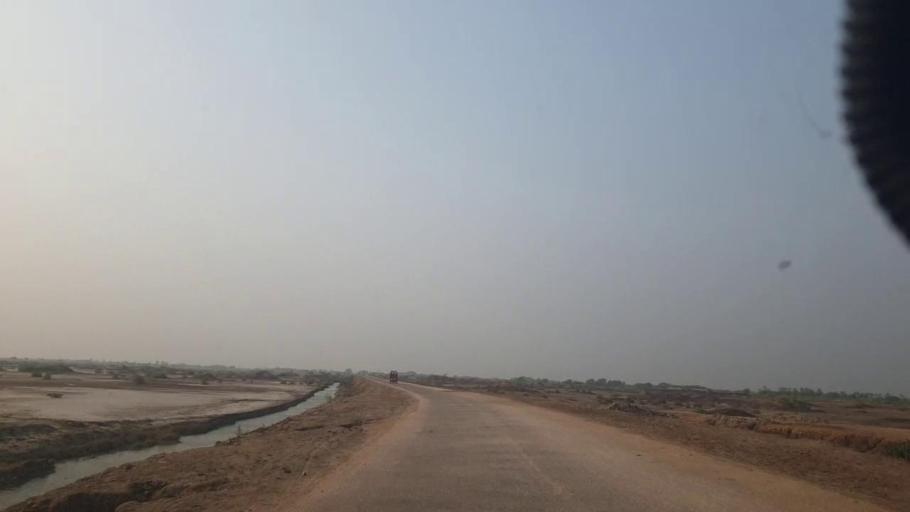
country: PK
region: Sindh
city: Bulri
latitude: 24.8532
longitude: 68.4043
